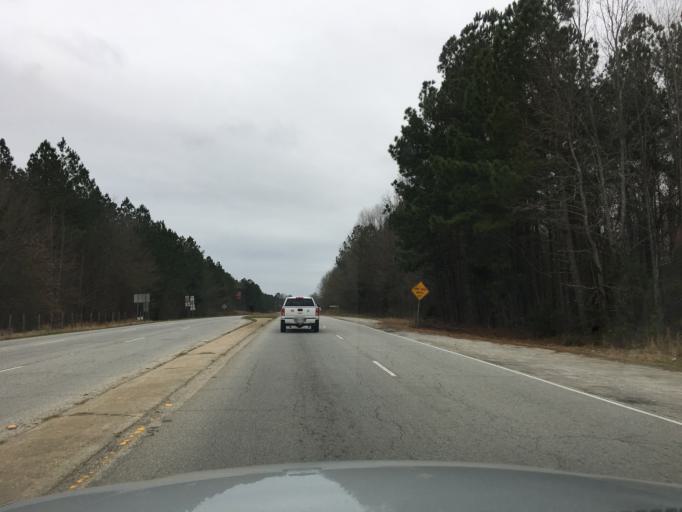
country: US
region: South Carolina
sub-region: Greenwood County
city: Greenwood
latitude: 34.1526
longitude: -82.1392
